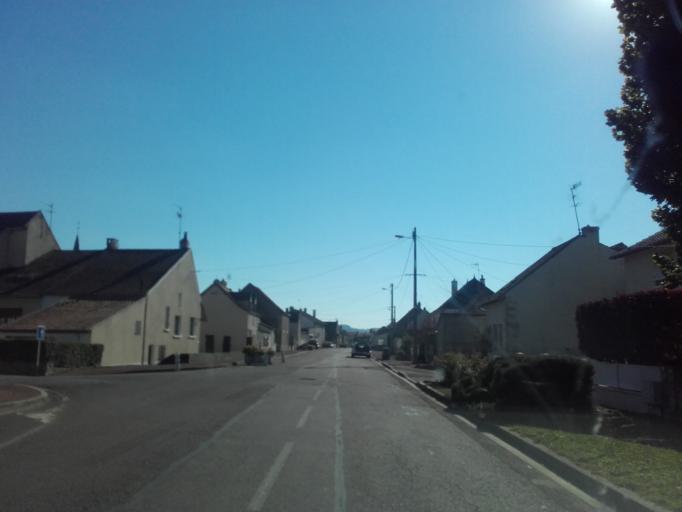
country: FR
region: Bourgogne
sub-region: Departement de la Cote-d'Or
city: Corpeau
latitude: 46.9310
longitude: 4.7534
